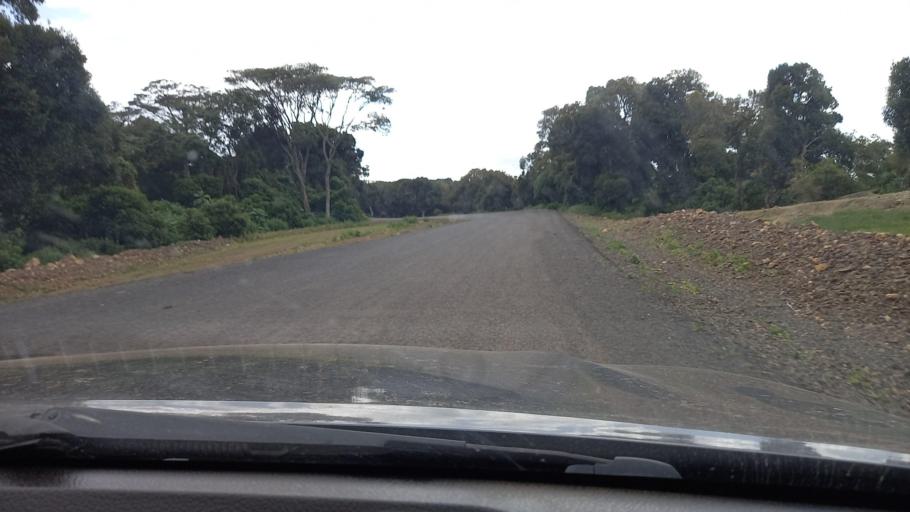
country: ET
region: Southern Nations, Nationalities, and People's Region
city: Mizan Teferi
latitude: 6.2082
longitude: 35.6091
